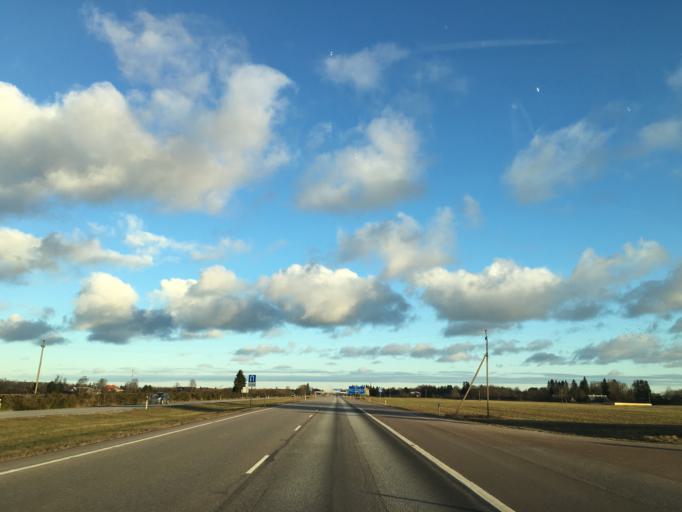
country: EE
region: Harju
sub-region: Saue linn
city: Saue
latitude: 59.3034
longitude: 24.5611
